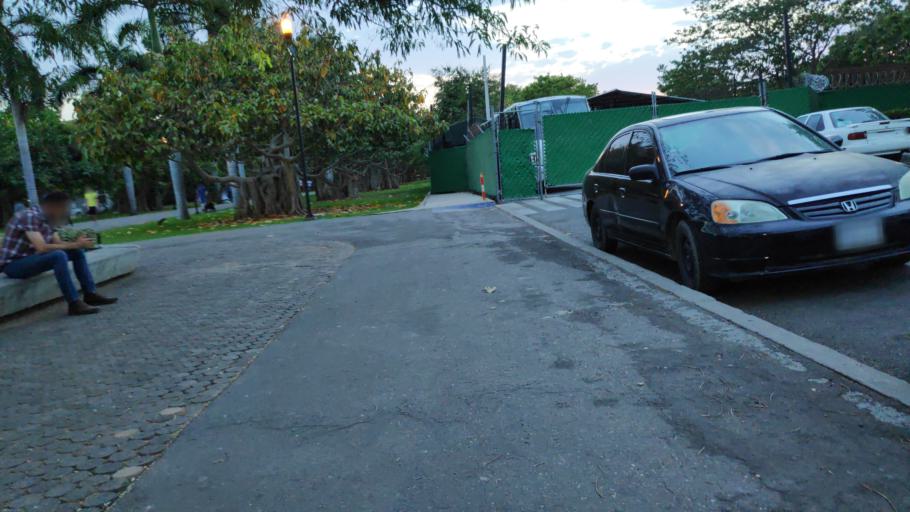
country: MX
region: Sinaloa
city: Culiacan
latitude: 24.8244
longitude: -107.3846
